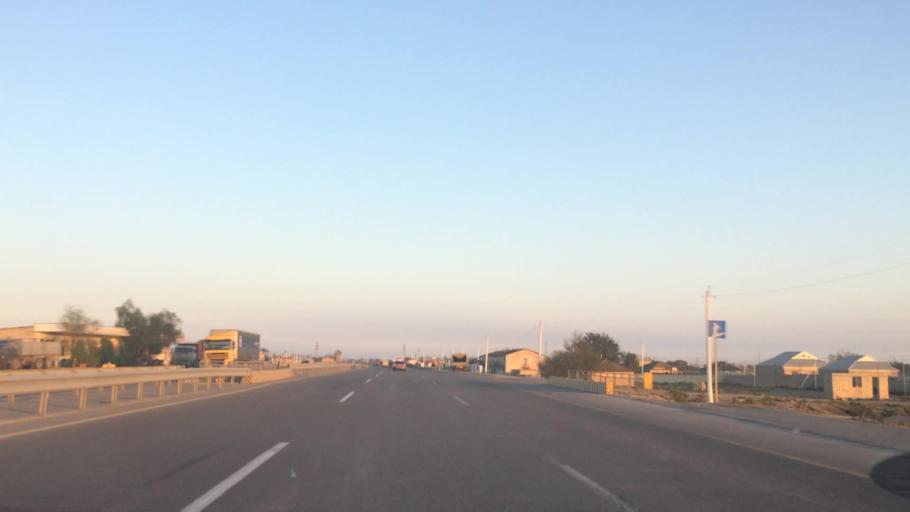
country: AZ
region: Baki
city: Qobustan
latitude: 39.9735
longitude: 49.2552
